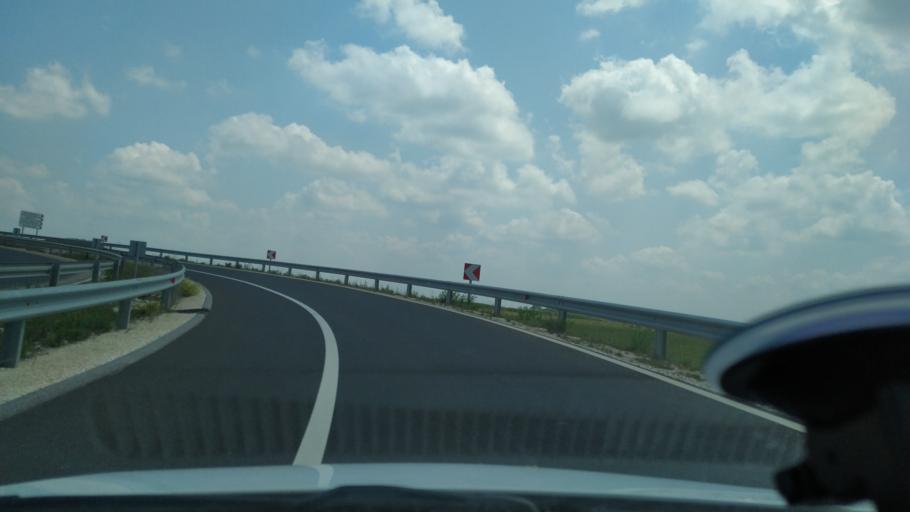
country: HU
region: Veszprem
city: Varpalota
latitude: 47.1960
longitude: 18.1858
